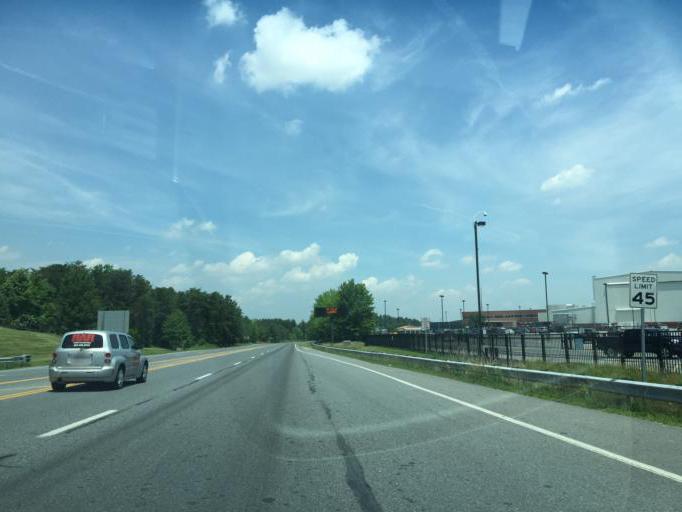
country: US
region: Maryland
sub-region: Howard County
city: Hanover
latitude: 39.1786
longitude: -76.6927
